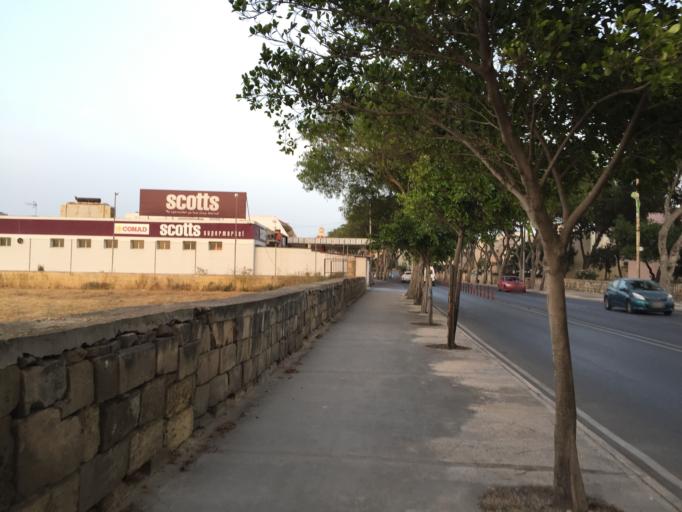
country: MT
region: Haz-Zabbar
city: Zabbar
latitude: 35.8721
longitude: 14.5276
